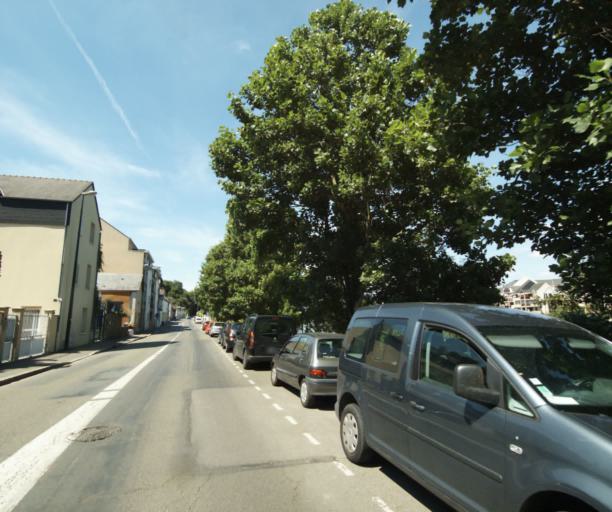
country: FR
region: Pays de la Loire
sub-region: Departement de la Mayenne
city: Laval
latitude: 48.0790
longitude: -0.7713
